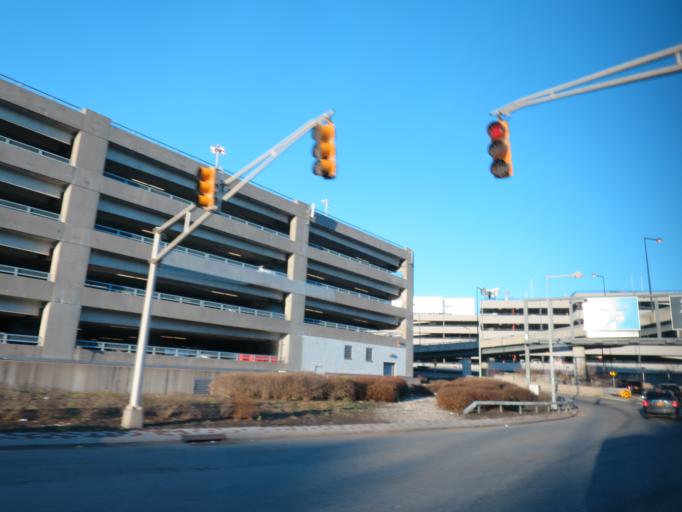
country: US
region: New York
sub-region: Nassau County
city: Inwood
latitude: 40.6452
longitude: -73.7807
